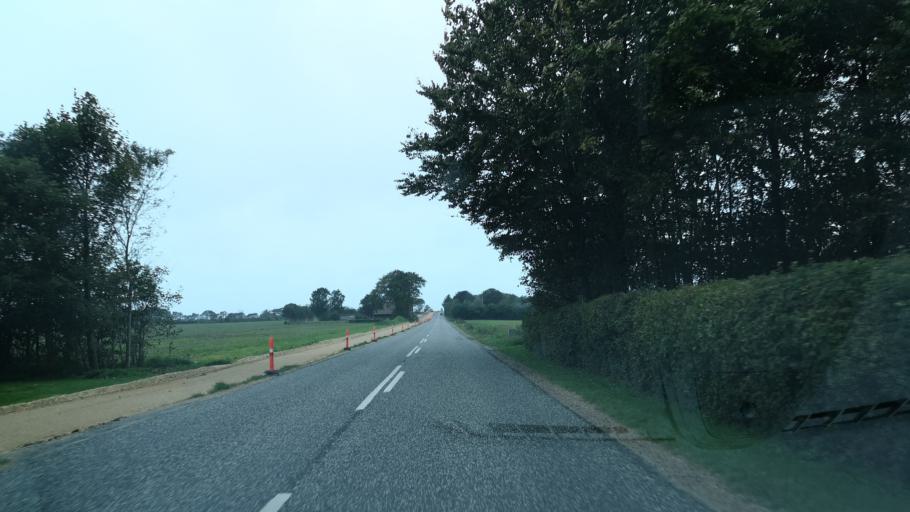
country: DK
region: Central Jutland
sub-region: Ringkobing-Skjern Kommune
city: Videbaek
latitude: 56.0529
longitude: 8.6483
